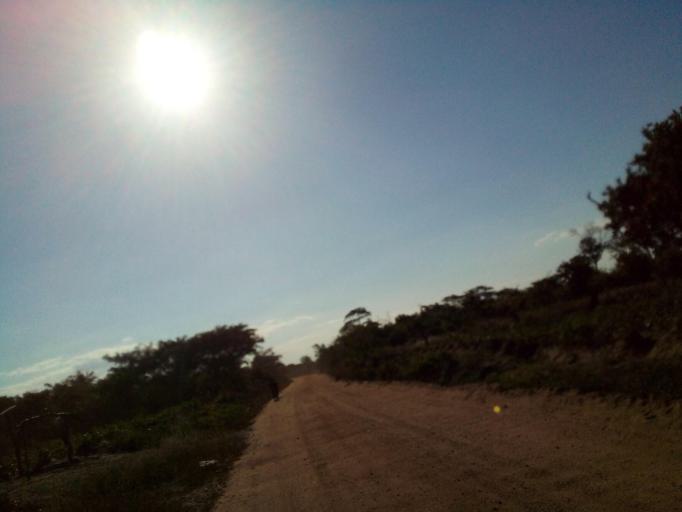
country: MZ
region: Zambezia
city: Quelimane
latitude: -17.4976
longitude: 36.5746
